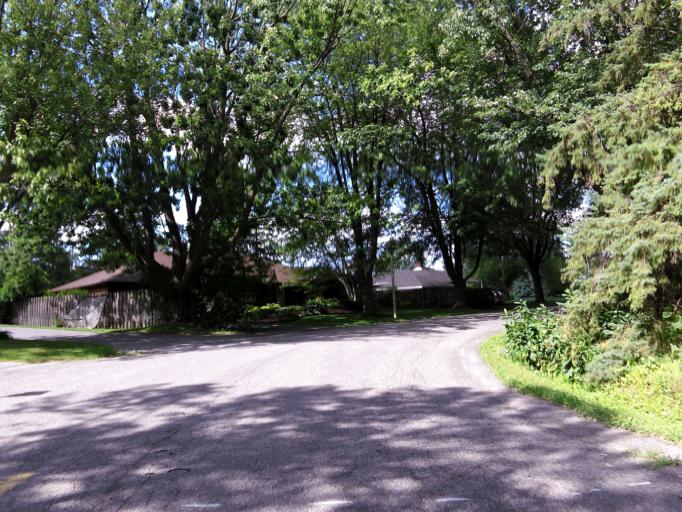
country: CA
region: Ontario
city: Ottawa
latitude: 45.3732
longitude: -75.7602
